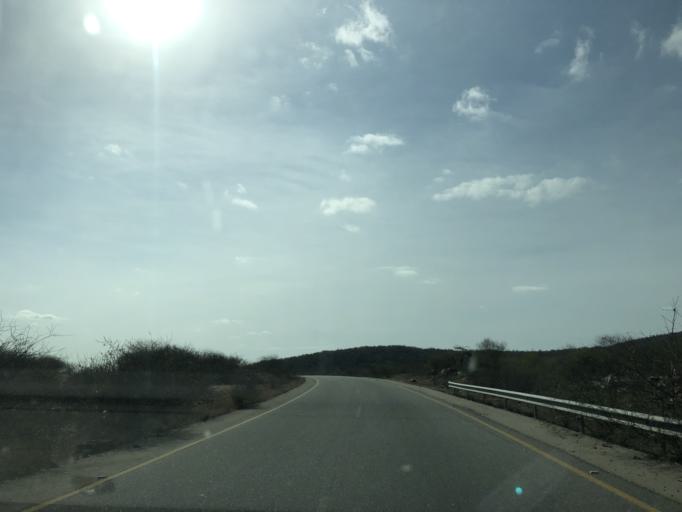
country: AO
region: Benguela
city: Benguela
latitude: -12.8934
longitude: 13.4922
